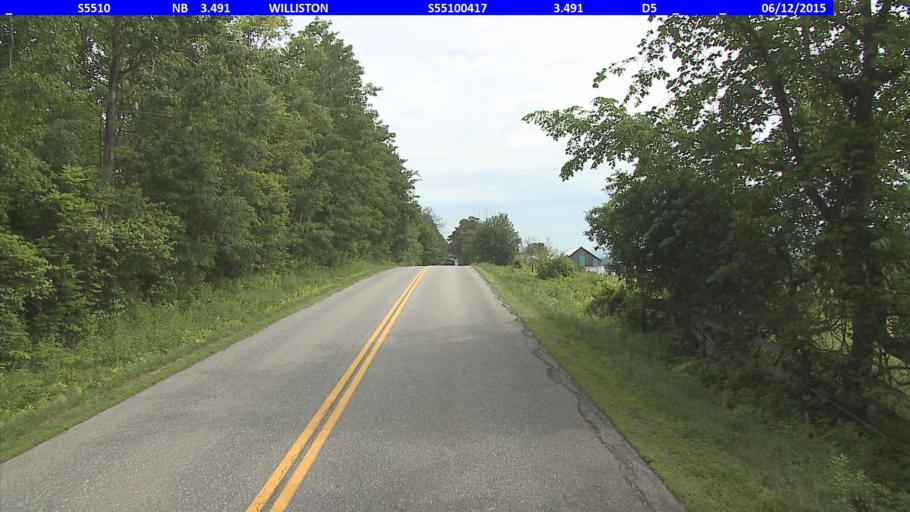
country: US
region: Vermont
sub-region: Chittenden County
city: Williston
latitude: 44.4203
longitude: -73.0814
